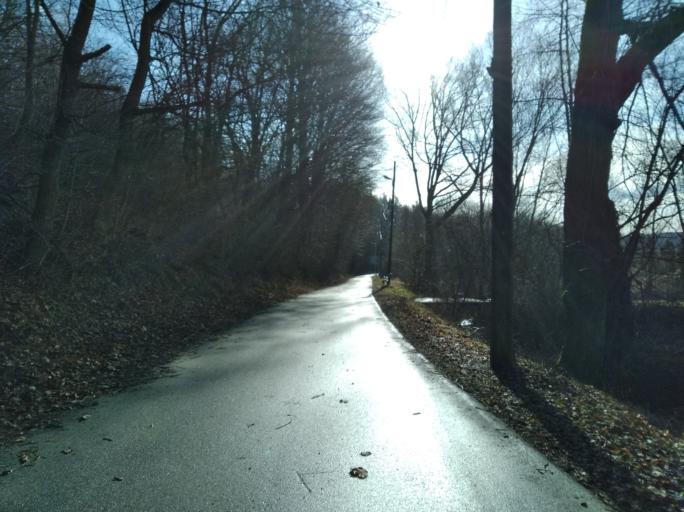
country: PL
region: Subcarpathian Voivodeship
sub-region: Powiat strzyzowski
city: Strzyzow
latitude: 49.8763
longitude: 21.7782
